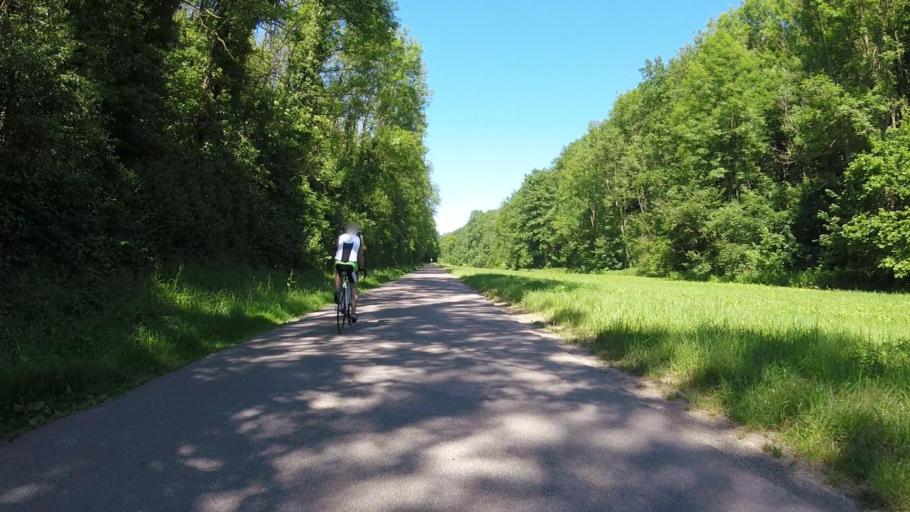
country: DE
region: Baden-Wuerttemberg
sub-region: Regierungsbezirk Stuttgart
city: Steinheim am der Murr
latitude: 48.9601
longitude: 9.2943
